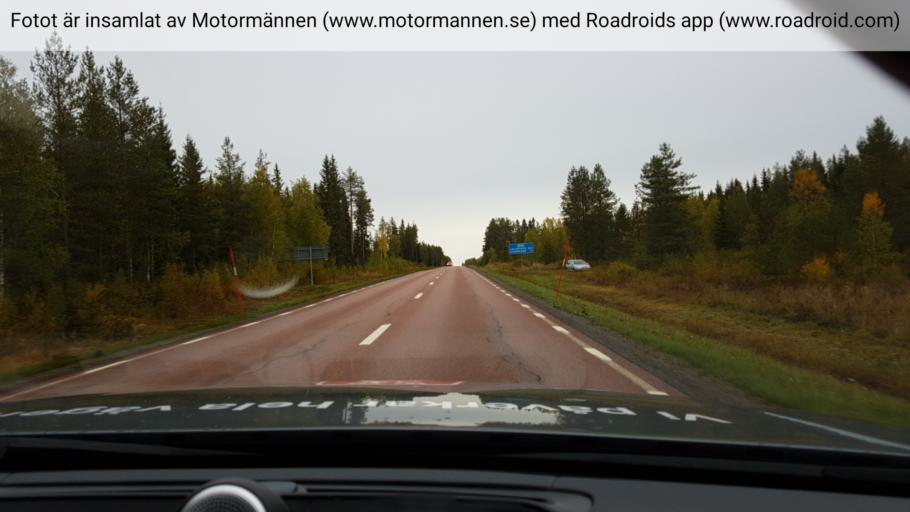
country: SE
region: Jaemtland
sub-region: Stroemsunds Kommun
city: Stroemsund
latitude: 63.7614
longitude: 15.5008
